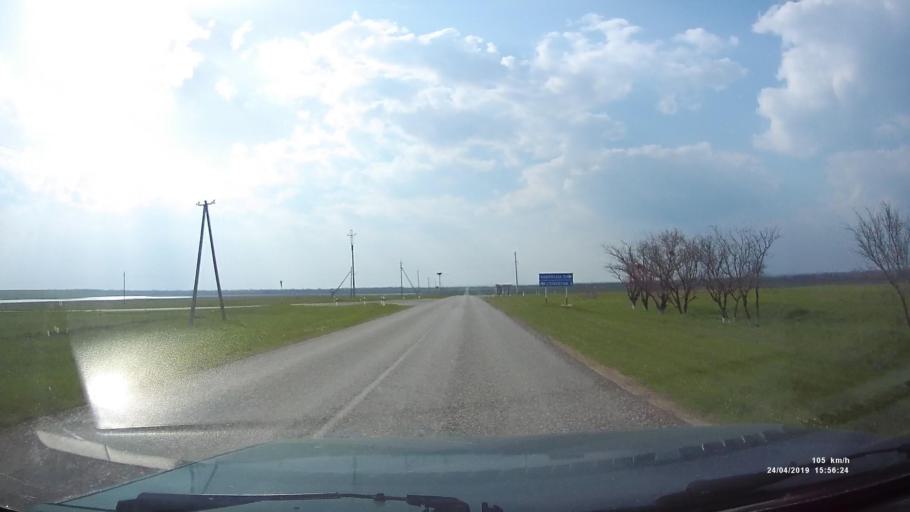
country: RU
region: Kalmykiya
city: Yashalta
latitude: 46.5975
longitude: 42.5293
